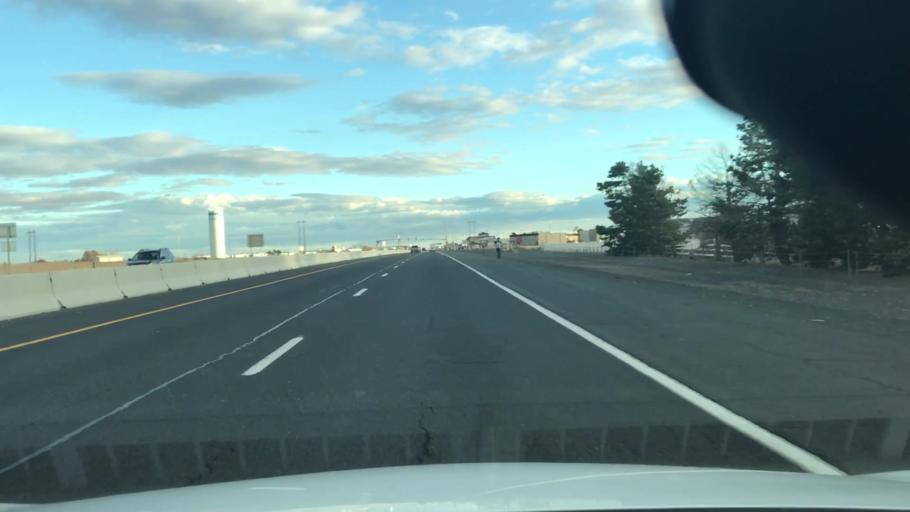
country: US
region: Washington
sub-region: Grant County
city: Moses Lake
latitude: 47.1093
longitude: -119.2557
